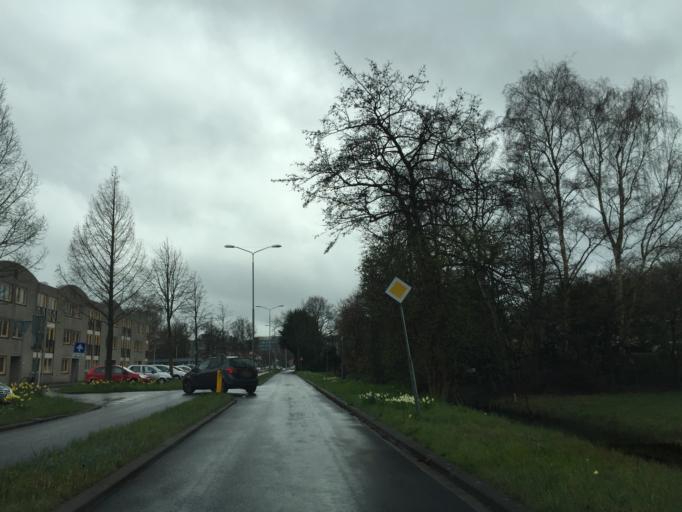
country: NL
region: South Holland
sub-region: Gemeente Leidschendam-Voorburg
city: Voorburg
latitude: 52.0854
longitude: 4.3977
